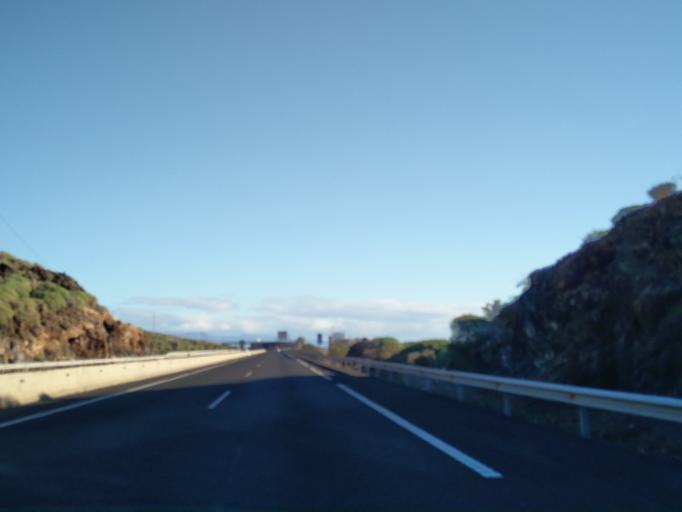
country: ES
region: Canary Islands
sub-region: Provincia de Santa Cruz de Tenerife
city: Fasnia
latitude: 28.2376
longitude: -16.4067
